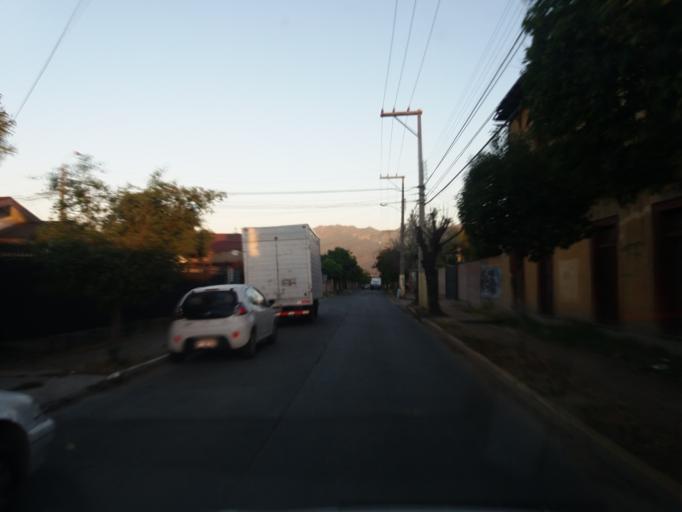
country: CL
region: Valparaiso
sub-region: Provincia de Quillota
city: Quillota
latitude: -32.8814
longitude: -71.2543
